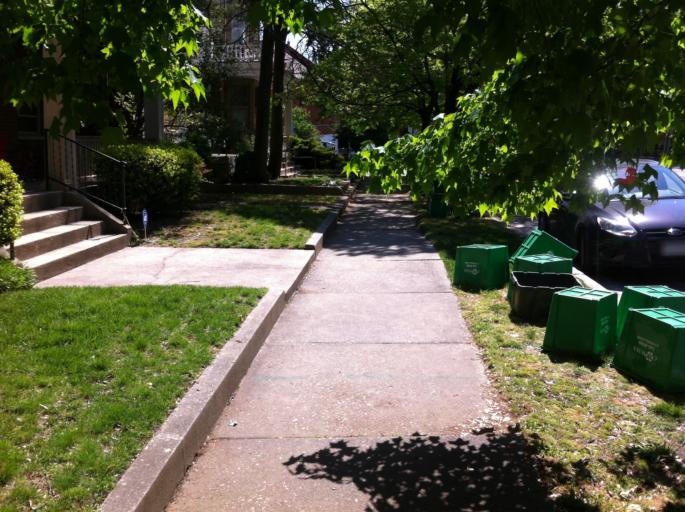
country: US
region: Virginia
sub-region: City of Richmond
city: Richmond
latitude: 37.5577
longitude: -77.4780
